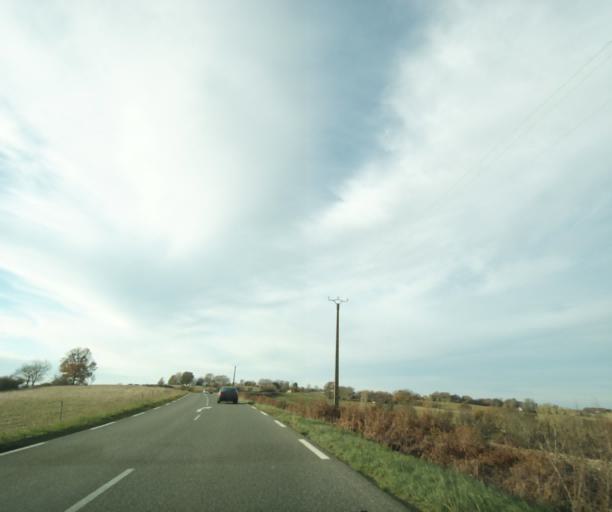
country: FR
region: Midi-Pyrenees
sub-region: Departement du Gers
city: Eauze
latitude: 43.7859
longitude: 0.1092
